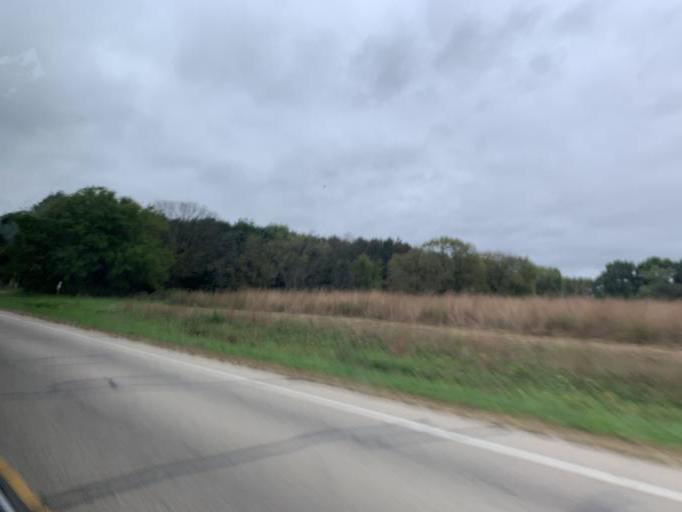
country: US
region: Wisconsin
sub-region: Grant County
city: Boscobel
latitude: 43.2053
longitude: -90.5873
